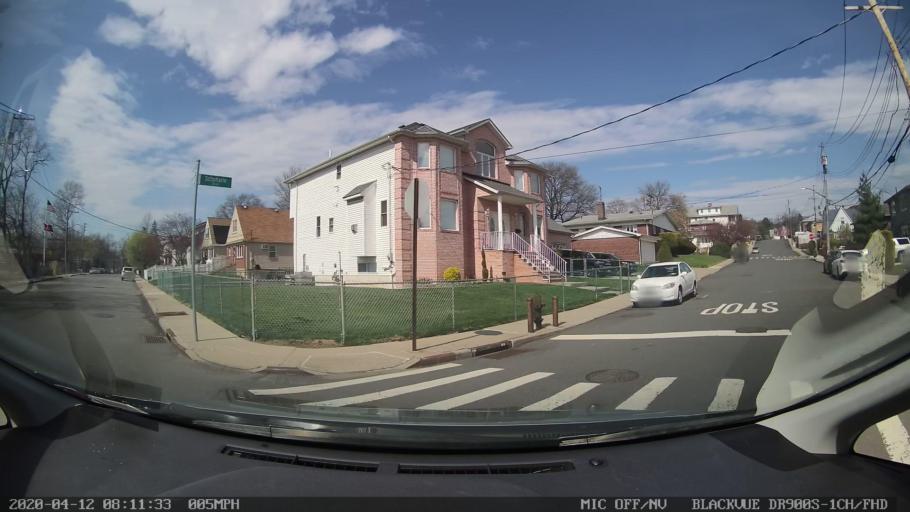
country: US
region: New Jersey
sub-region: Hudson County
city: Bayonne
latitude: 40.6137
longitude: -74.1040
